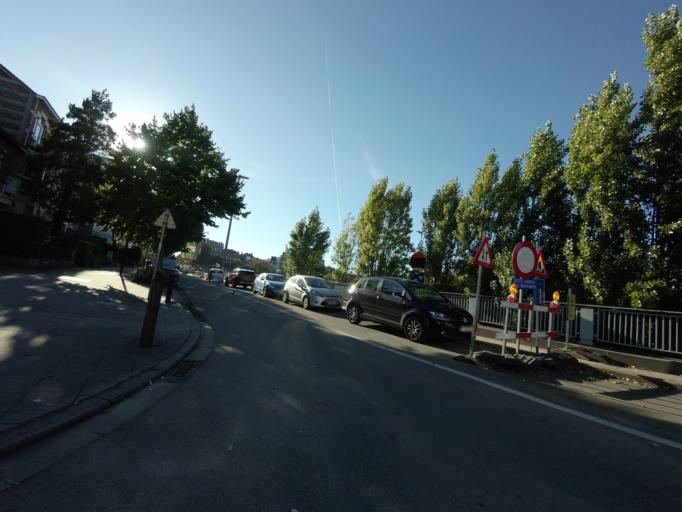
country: BE
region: Brussels Capital
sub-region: Bruxelles-Capitale
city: Brussels
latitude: 50.8494
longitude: 4.4045
